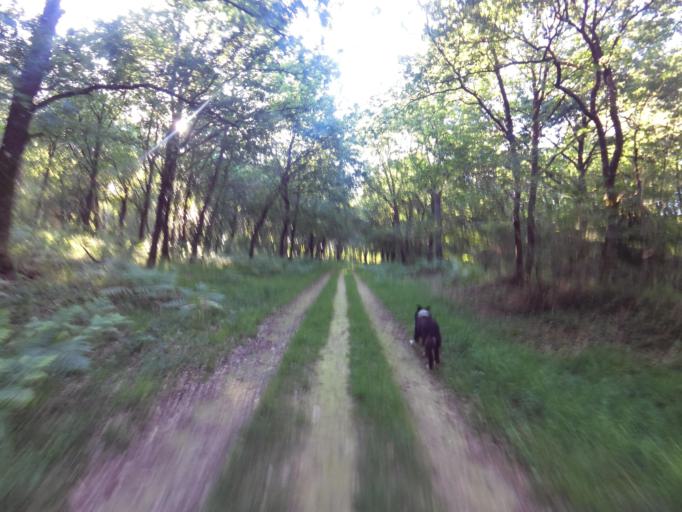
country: FR
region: Brittany
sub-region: Departement du Morbihan
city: Molac
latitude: 47.7436
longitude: -2.4326
